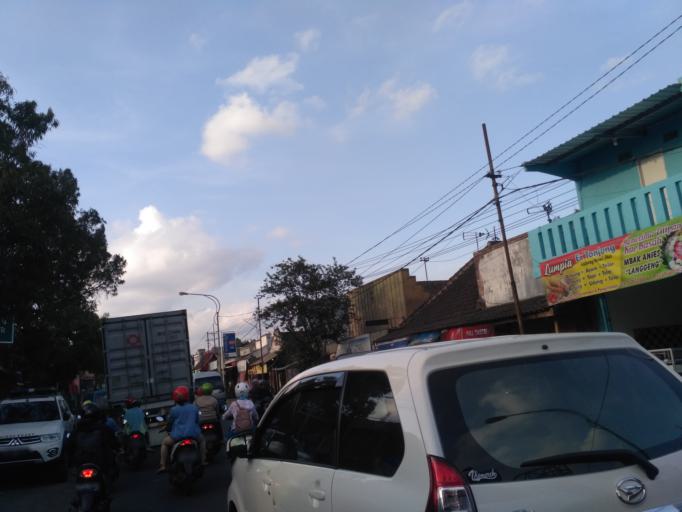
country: ID
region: East Java
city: Kebonsari
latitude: -8.0258
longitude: 112.6166
